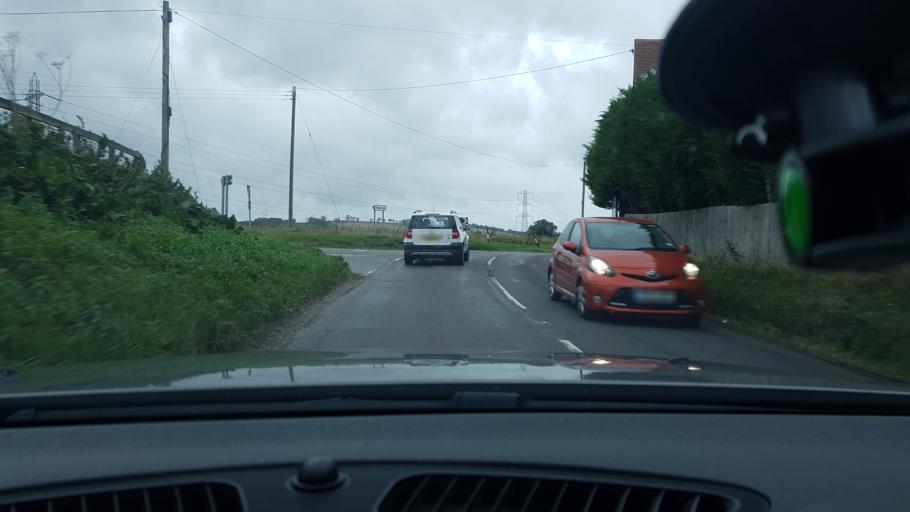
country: GB
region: England
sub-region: Wiltshire
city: Great Bedwyn
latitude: 51.3442
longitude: -1.5984
